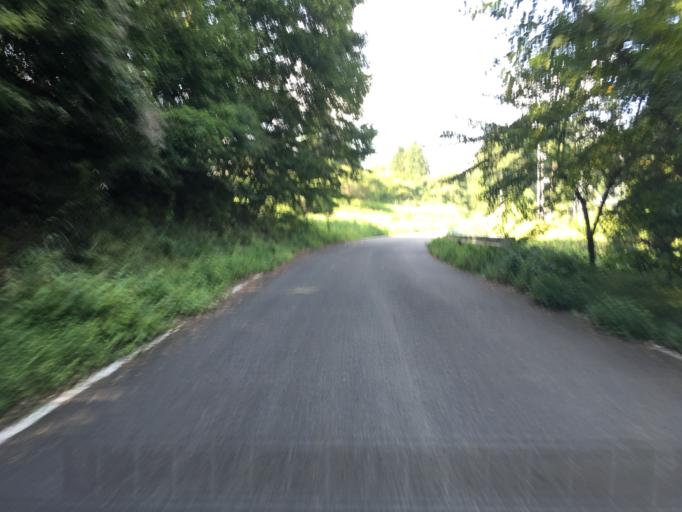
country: JP
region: Fukushima
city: Nihommatsu
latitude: 37.6063
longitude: 140.3854
